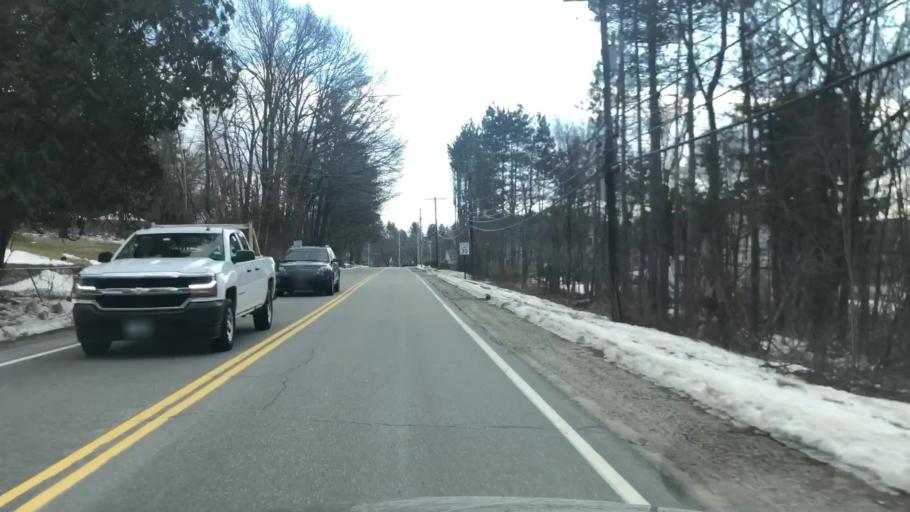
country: US
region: New Hampshire
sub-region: Hillsborough County
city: Milford
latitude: 42.8440
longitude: -71.6594
